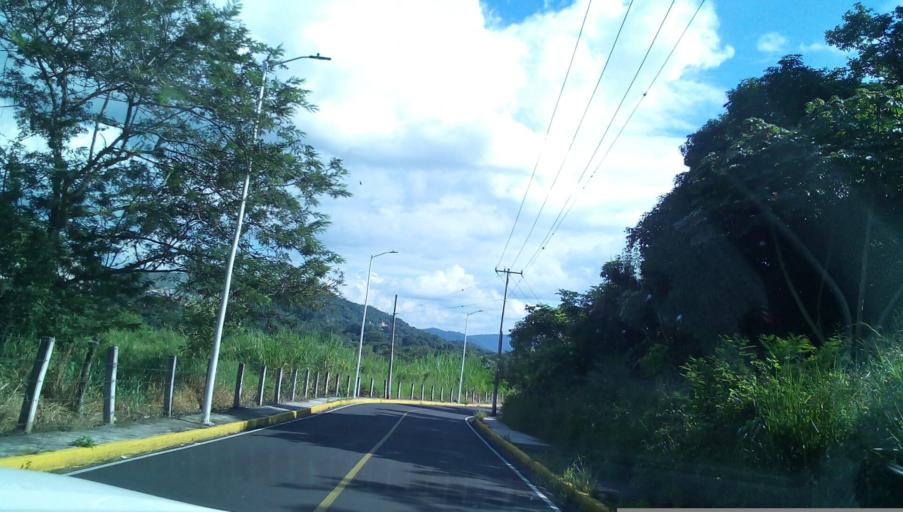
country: MX
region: Veracruz
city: Cordoba
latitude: 18.8982
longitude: -96.9218
